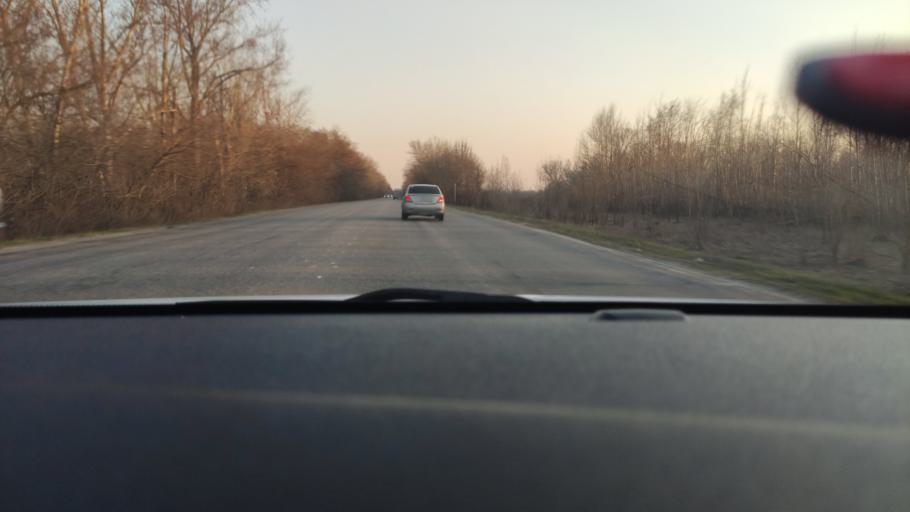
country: RU
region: Voronezj
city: Maslovka
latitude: 51.4854
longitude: 39.3074
